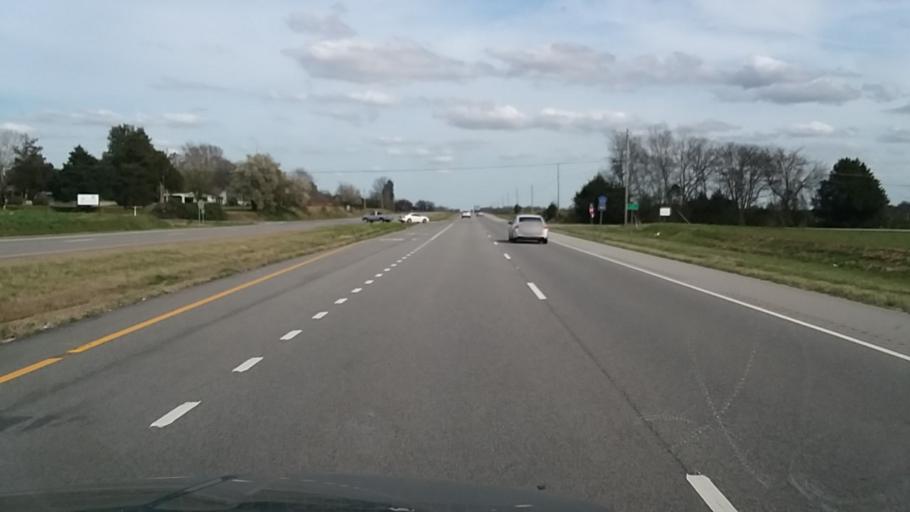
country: US
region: Alabama
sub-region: Colbert County
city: Muscle Shoals
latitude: 34.6847
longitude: -87.5654
